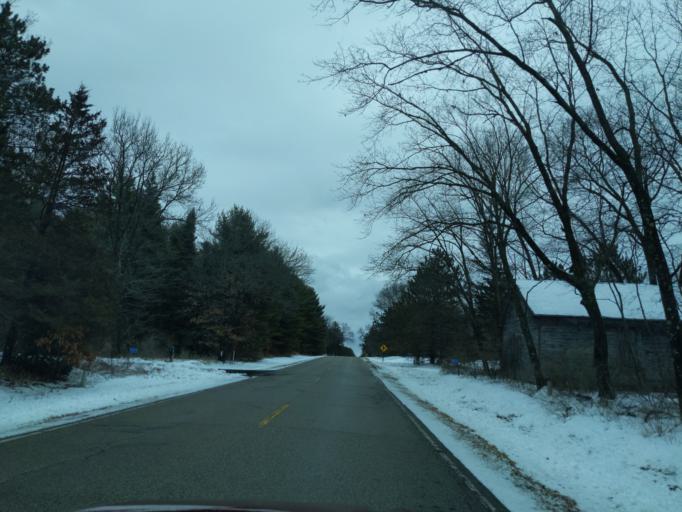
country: US
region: Wisconsin
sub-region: Marquette County
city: Montello
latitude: 43.9197
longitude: -89.3175
